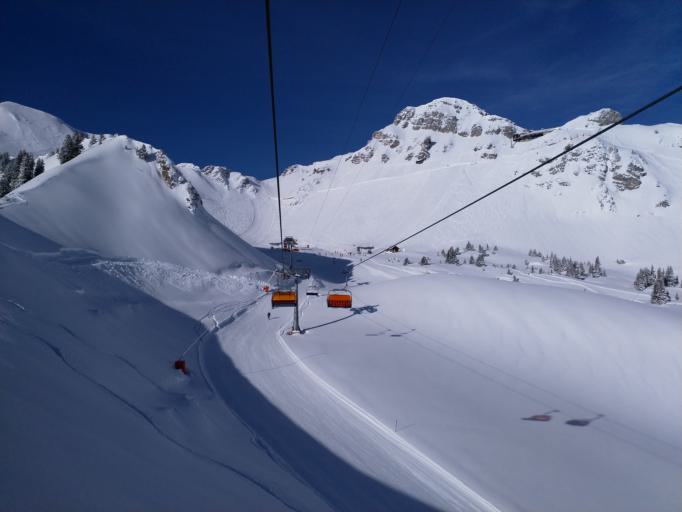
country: CH
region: Bern
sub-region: Obersimmental-Saanen District
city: Saanen
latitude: 46.4566
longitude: 7.2115
